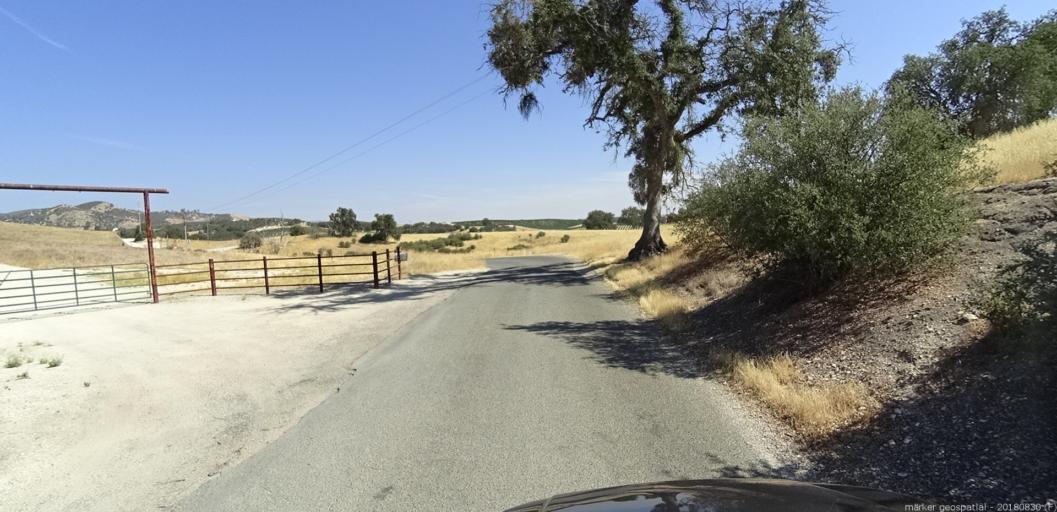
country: US
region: California
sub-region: Monterey County
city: King City
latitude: 36.0104
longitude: -121.1562
